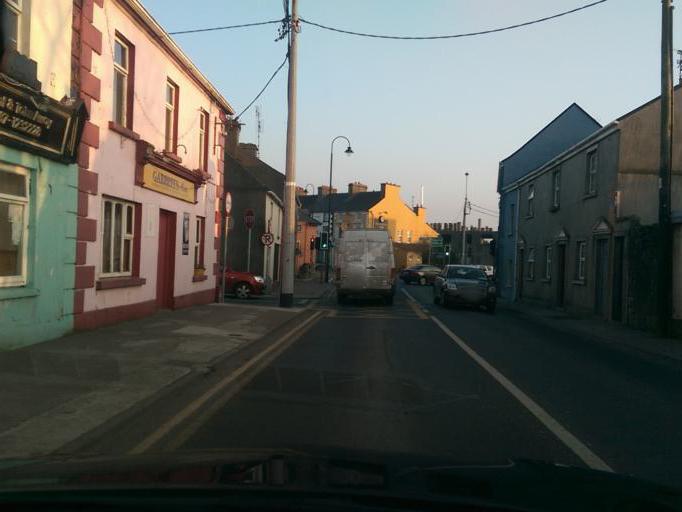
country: IE
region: Connaught
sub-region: County Galway
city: Loughrea
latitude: 53.1996
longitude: -8.5742
